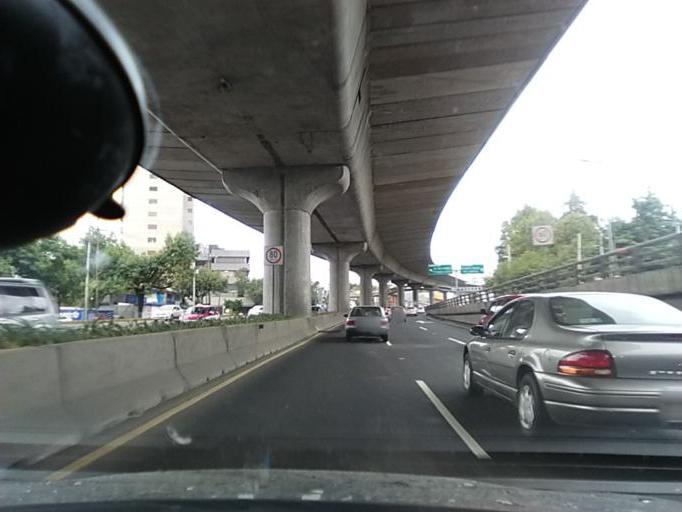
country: MX
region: Mexico City
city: Magdalena Contreras
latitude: 19.3275
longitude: -99.2124
